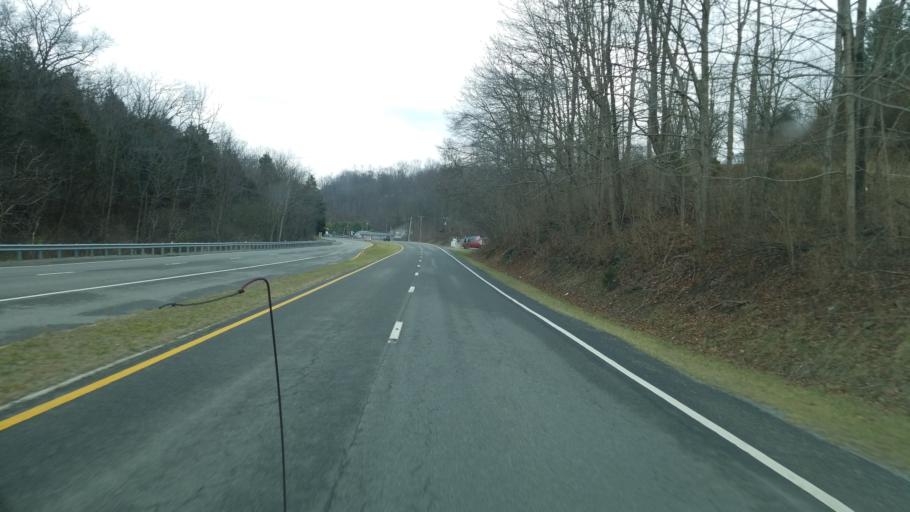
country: US
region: Virginia
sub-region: Giles County
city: Pearisburg
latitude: 37.2705
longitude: -80.7292
